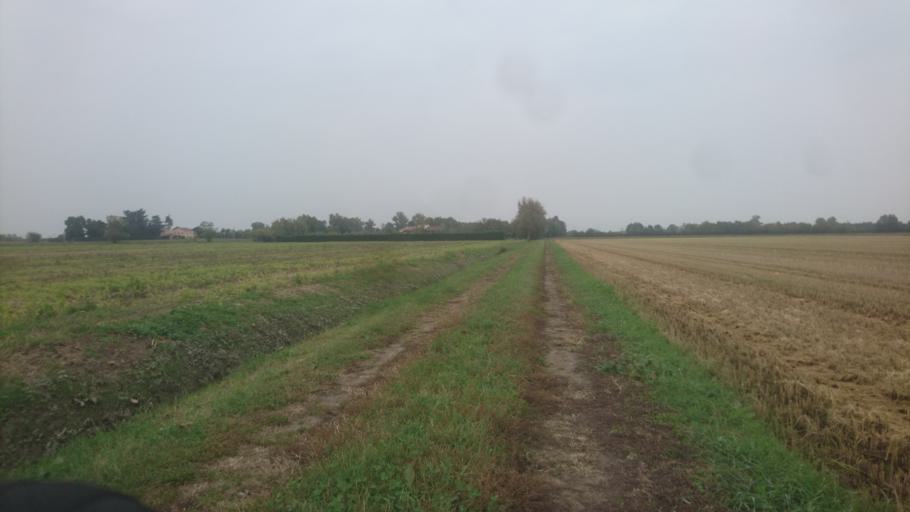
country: IT
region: Veneto
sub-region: Provincia di Vicenza
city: Grumolo delle Abbadesse
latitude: 45.5499
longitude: 11.6707
